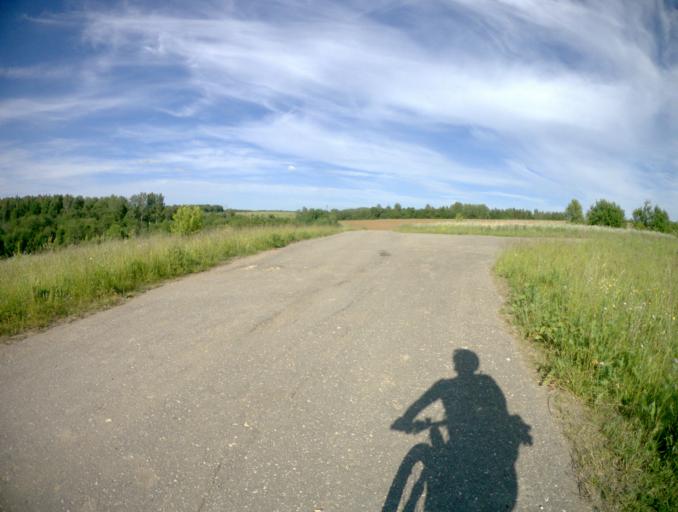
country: RU
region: Vladimir
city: Vorsha
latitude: 56.1725
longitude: 40.1723
